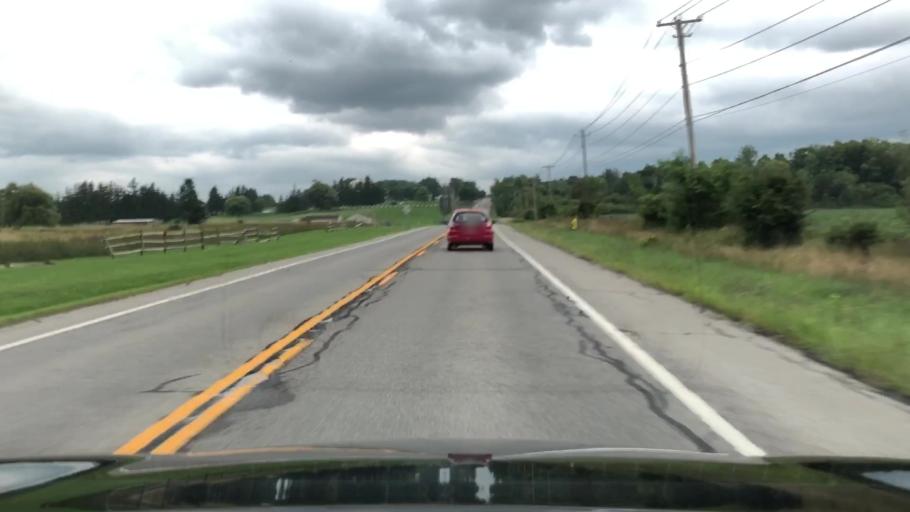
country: US
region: New York
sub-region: Erie County
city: Orchard Park
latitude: 42.7776
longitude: -78.6969
